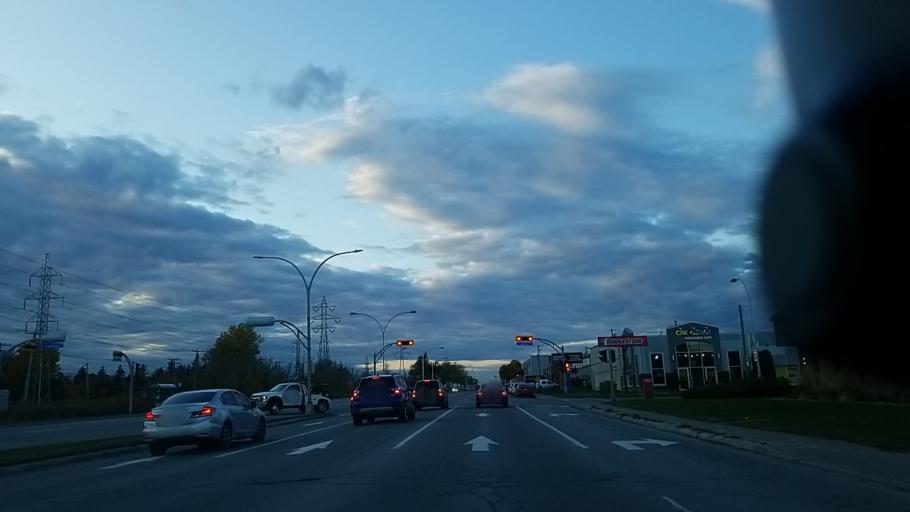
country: CA
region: Quebec
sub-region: Laval
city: Laval
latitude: 45.5769
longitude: -73.7266
